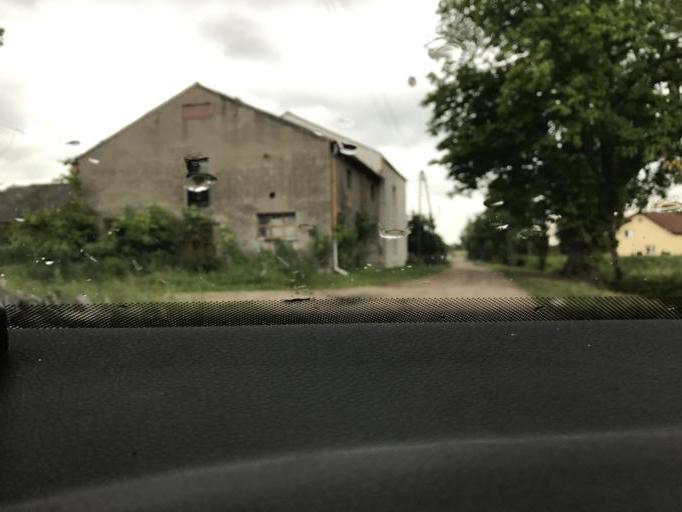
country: PL
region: Pomeranian Voivodeship
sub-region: Powiat gdanski
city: Pruszcz Gdanski
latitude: 54.2803
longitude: 18.6490
